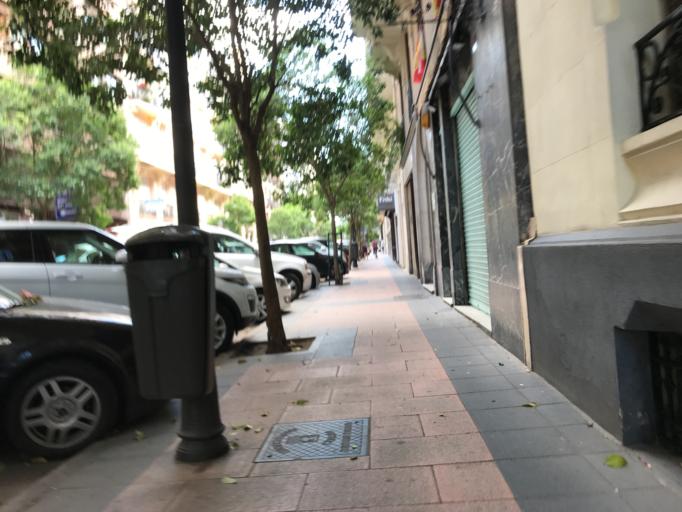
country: ES
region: Madrid
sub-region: Provincia de Madrid
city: Salamanca
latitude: 40.4232
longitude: -3.6829
